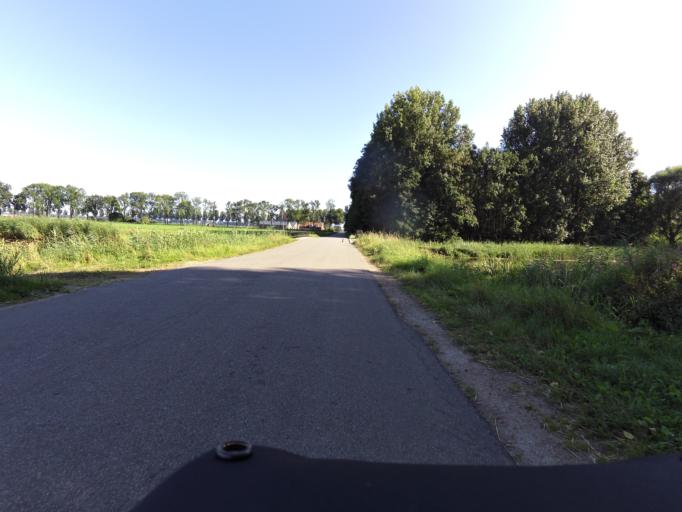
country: NL
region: South Holland
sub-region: Gemeente Dordrecht
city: Dordrecht
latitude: 51.7636
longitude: 4.6920
